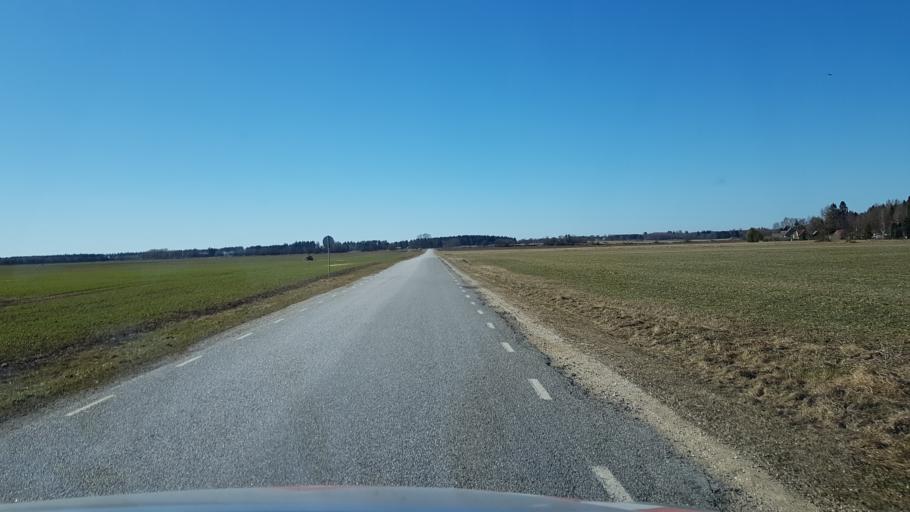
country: EE
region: Laeaene-Virumaa
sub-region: Viru-Nigula vald
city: Kunda
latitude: 59.3972
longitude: 26.5586
